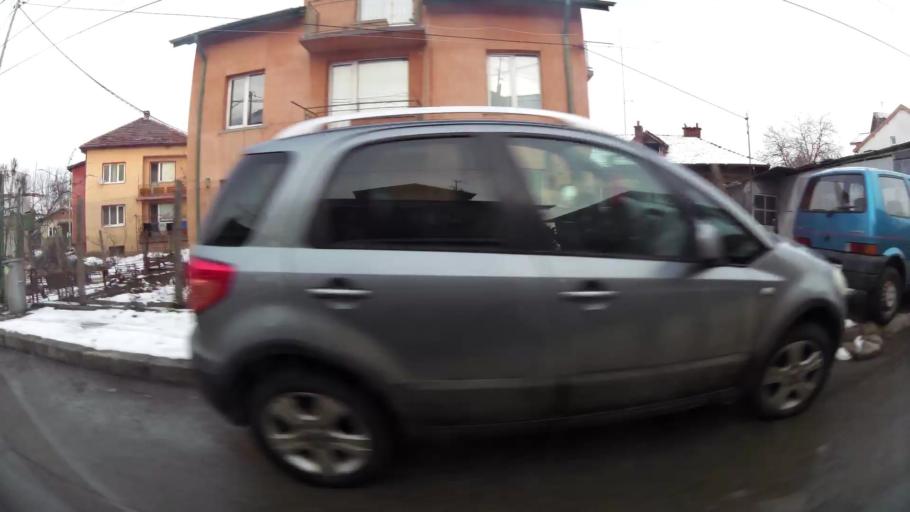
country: BG
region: Sofia-Capital
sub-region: Stolichna Obshtina
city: Sofia
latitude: 42.7220
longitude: 23.3457
